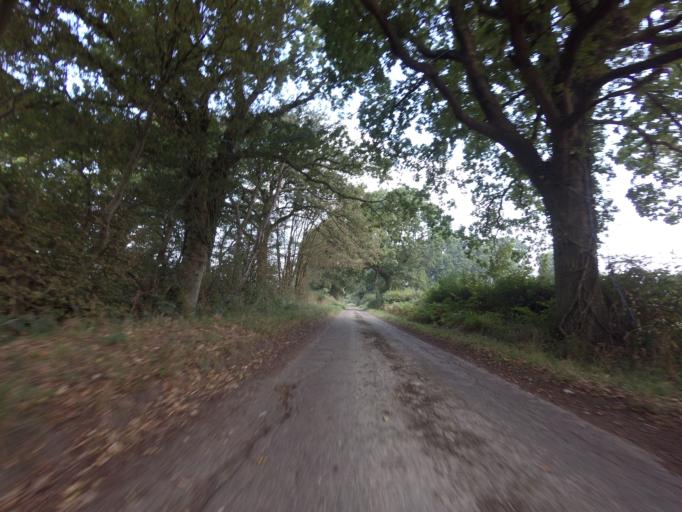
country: GB
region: England
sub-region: Kent
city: Tenterden
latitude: 51.1122
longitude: 0.7772
